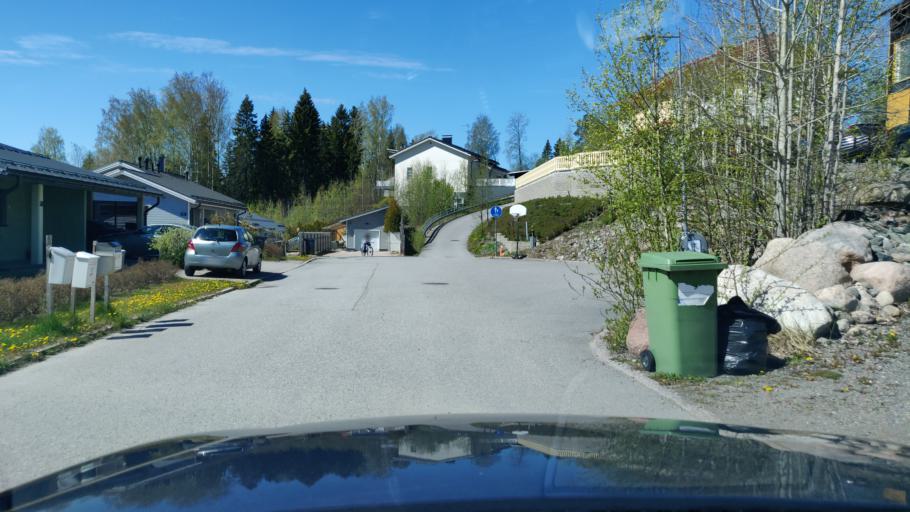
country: FI
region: Uusimaa
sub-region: Helsinki
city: Nurmijaervi
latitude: 60.3617
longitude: 24.7506
